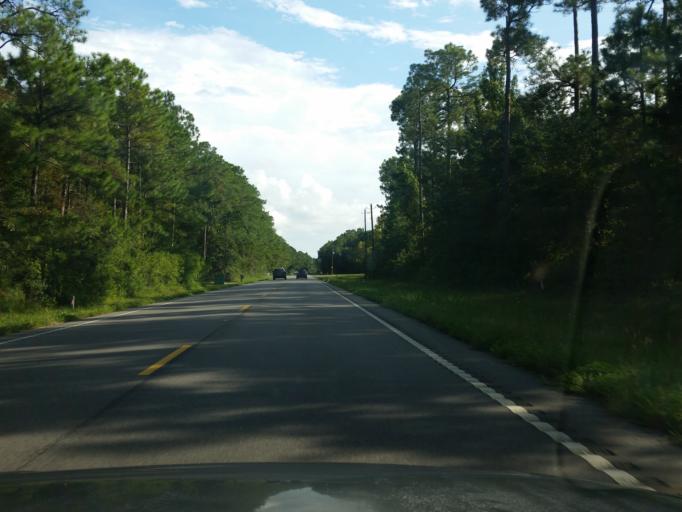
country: US
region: Alabama
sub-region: Mobile County
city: Bayou La Batre
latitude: 30.4068
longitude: -88.1076
